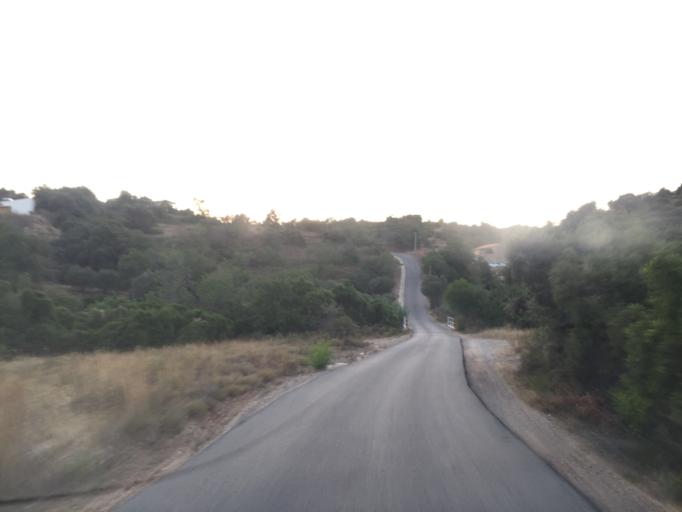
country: PT
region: Faro
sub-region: Loule
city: Almancil
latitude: 37.1033
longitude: -8.0156
